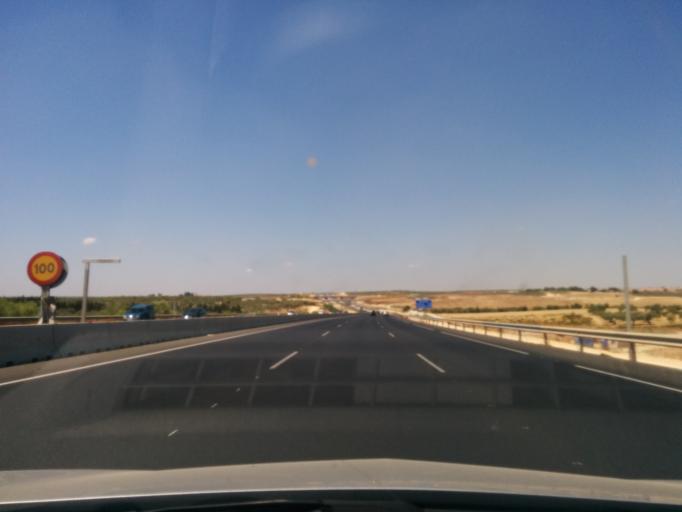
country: ES
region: Andalusia
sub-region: Provincia de Sevilla
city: Bormujos
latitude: 37.3737
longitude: -6.0874
